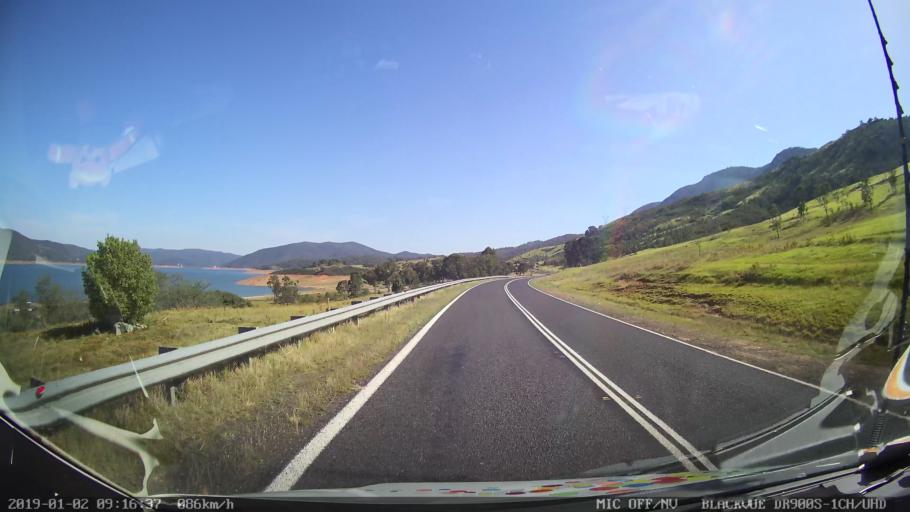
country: AU
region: New South Wales
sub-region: Tumut Shire
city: Tumut
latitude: -35.4512
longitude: 148.2844
